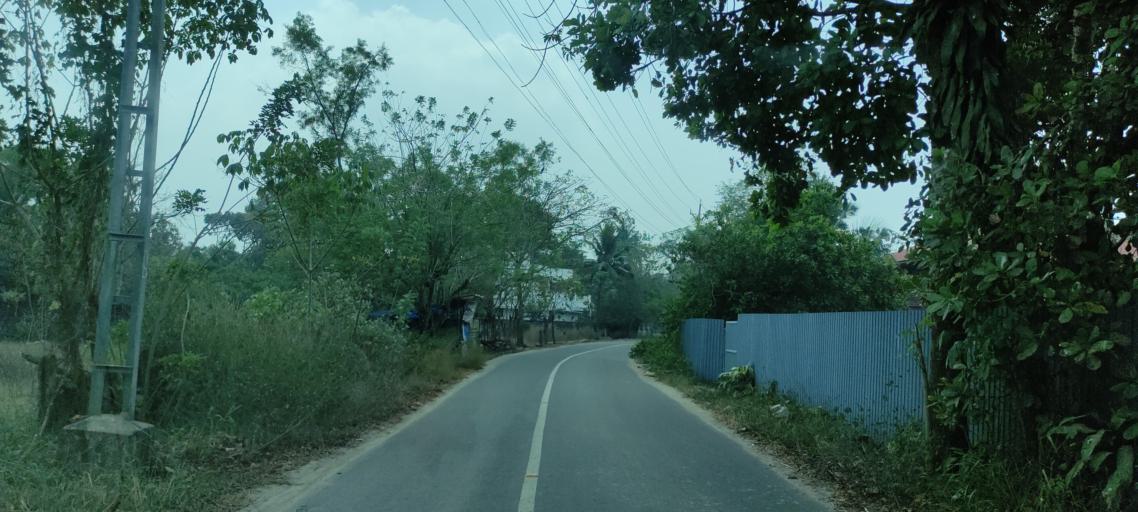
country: IN
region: Kerala
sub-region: Alappuzha
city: Alleppey
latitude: 9.5735
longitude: 76.3392
